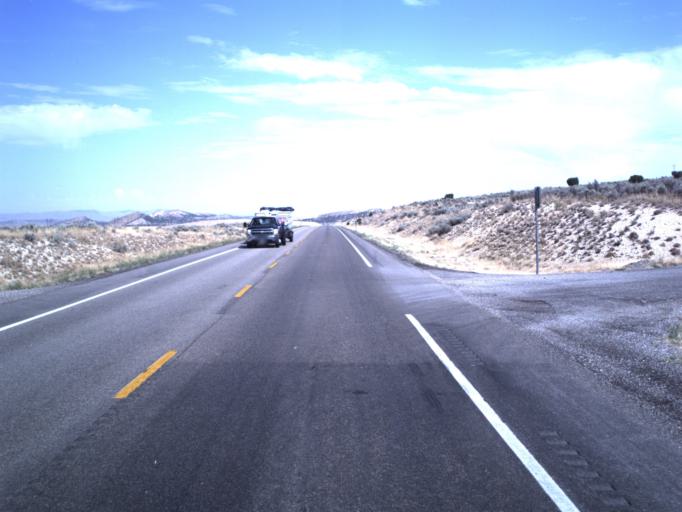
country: US
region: Utah
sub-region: Sanpete County
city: Gunnison
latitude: 39.3210
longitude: -111.9076
